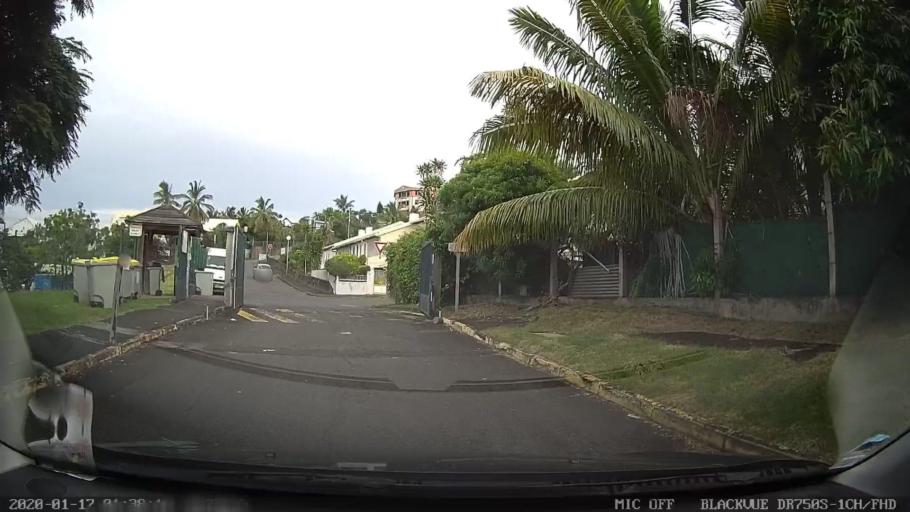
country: RE
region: Reunion
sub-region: Reunion
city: Saint-Denis
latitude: -20.9042
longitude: 55.4866
